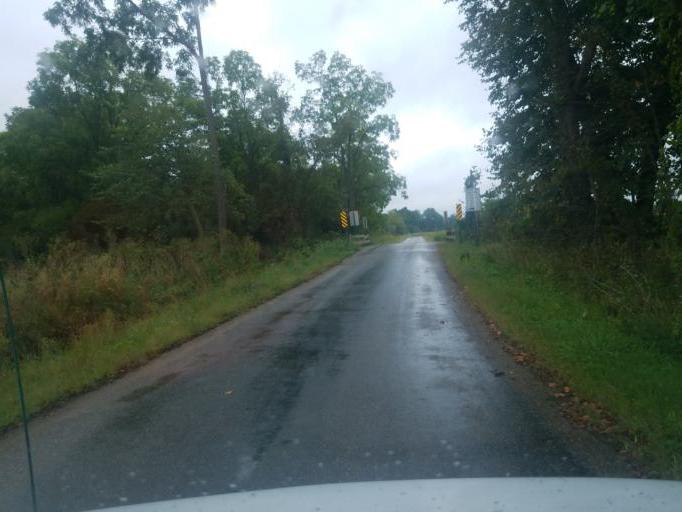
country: US
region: Ohio
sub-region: Wayne County
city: West Salem
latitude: 40.9443
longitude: -82.1169
